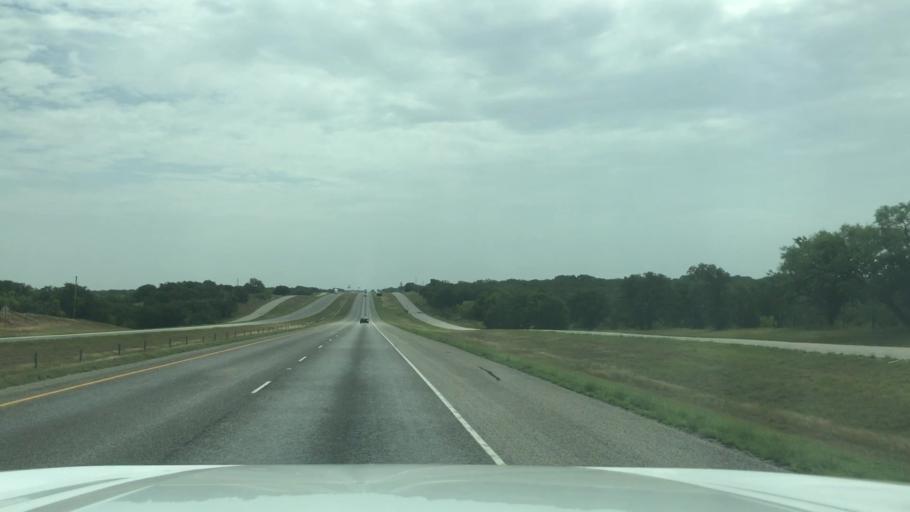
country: US
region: Texas
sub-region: Eastland County
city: Cisco
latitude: 32.3754
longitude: -99.0349
